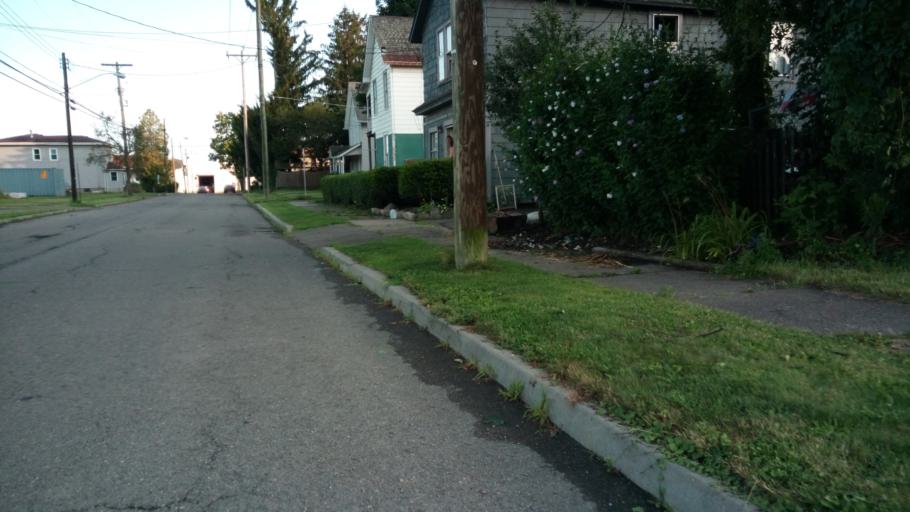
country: US
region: New York
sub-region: Chemung County
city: Elmira
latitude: 42.0979
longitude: -76.8117
